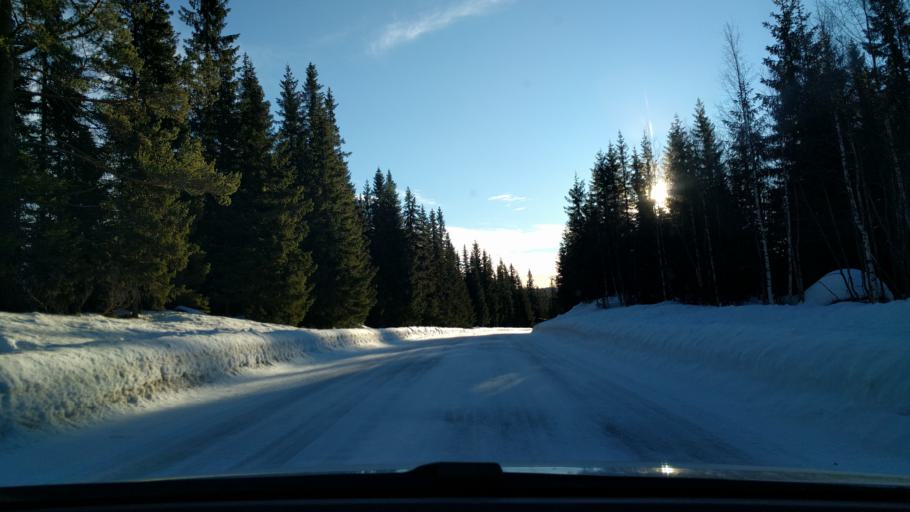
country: NO
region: Hedmark
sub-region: Trysil
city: Innbygda
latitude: 61.1062
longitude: 12.1207
